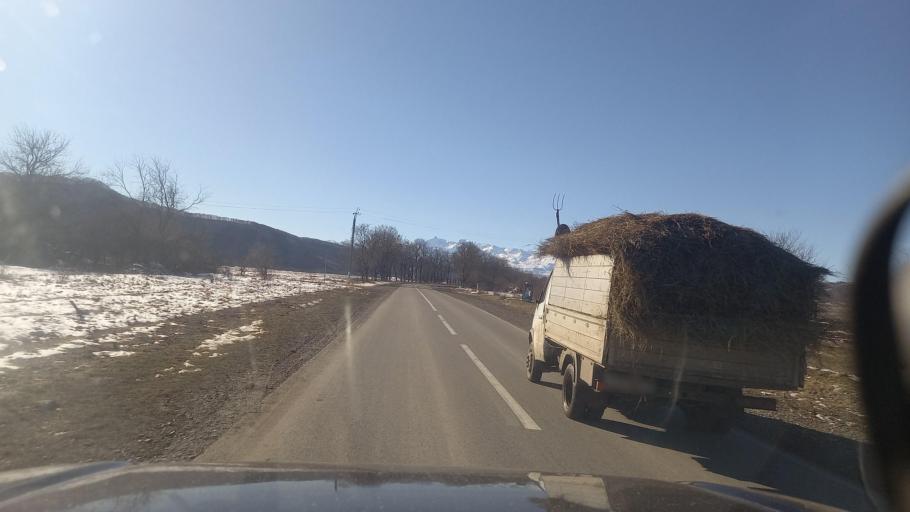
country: RU
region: Kabardino-Balkariya
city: Urukh
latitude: 43.2533
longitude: 43.9763
